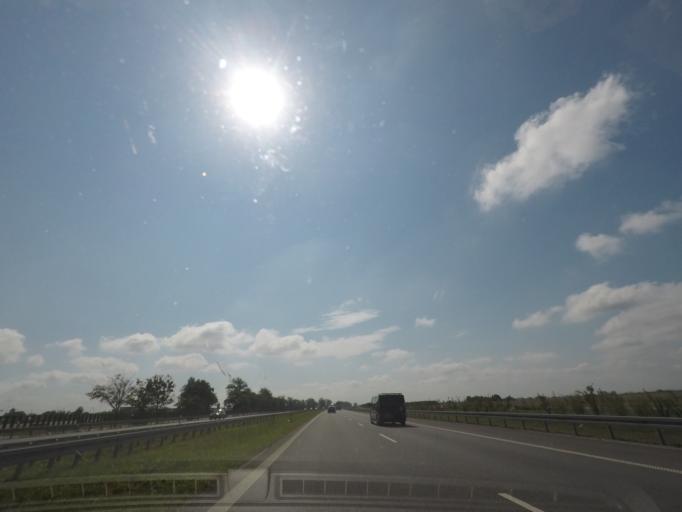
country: PL
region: Kujawsko-Pomorskie
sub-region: Powiat aleksandrowski
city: Raciazek
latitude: 52.8456
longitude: 18.7871
